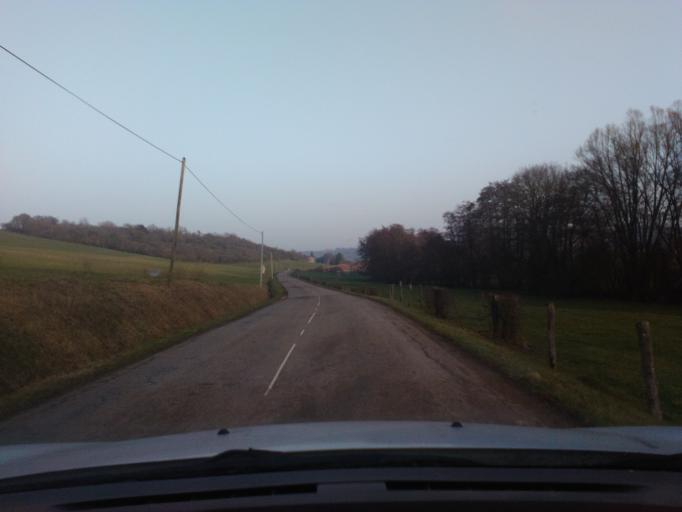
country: FR
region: Lorraine
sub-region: Departement des Vosges
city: Vittel
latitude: 48.2769
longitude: 6.0255
